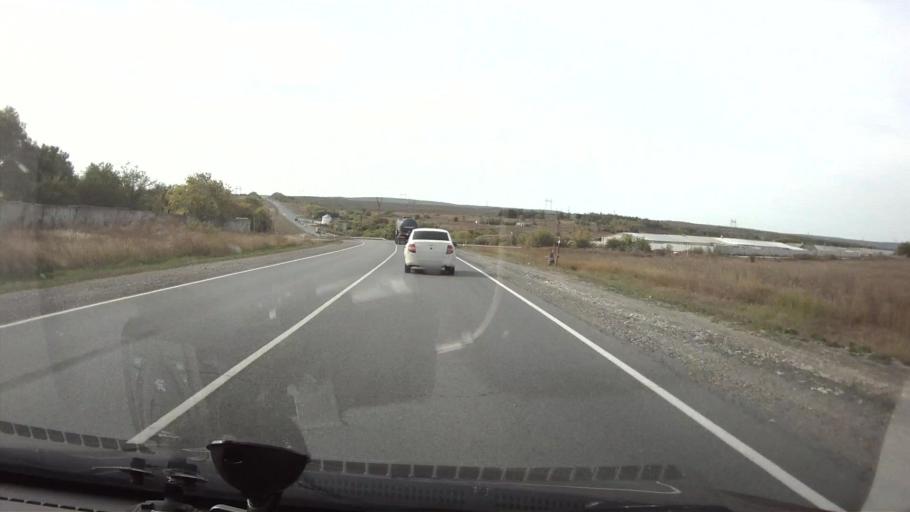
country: RU
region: Saratov
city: Tersa
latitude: 52.0965
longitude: 47.5359
